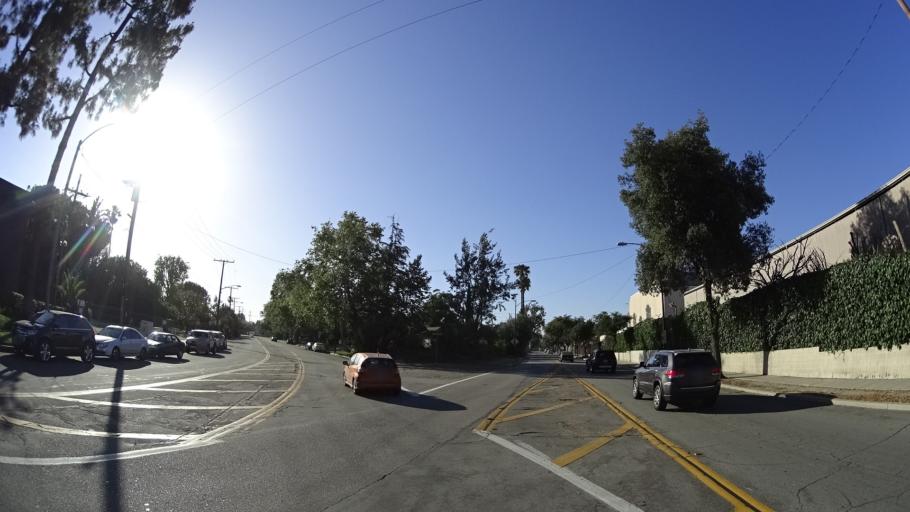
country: US
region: California
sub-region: Los Angeles County
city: Universal City
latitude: 34.1577
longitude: -118.3468
